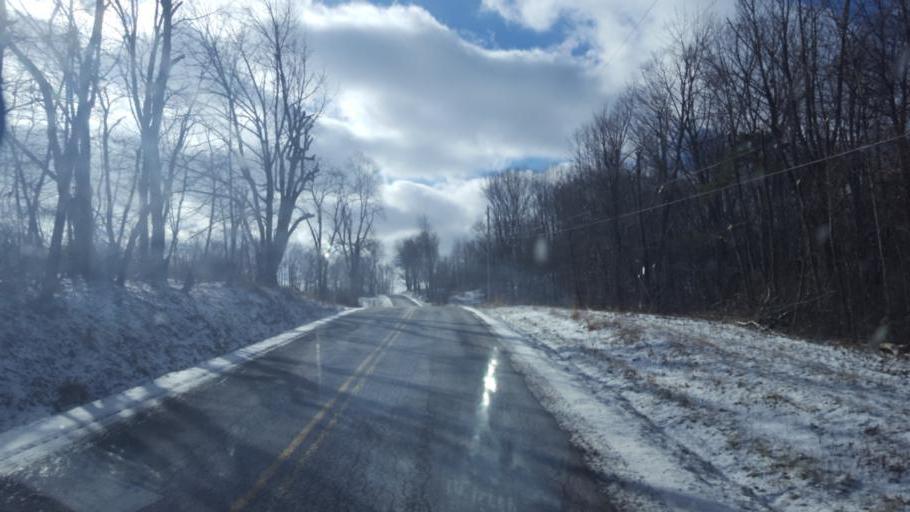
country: US
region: Ohio
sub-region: Coshocton County
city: West Lafayette
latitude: 40.3482
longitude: -81.7757
